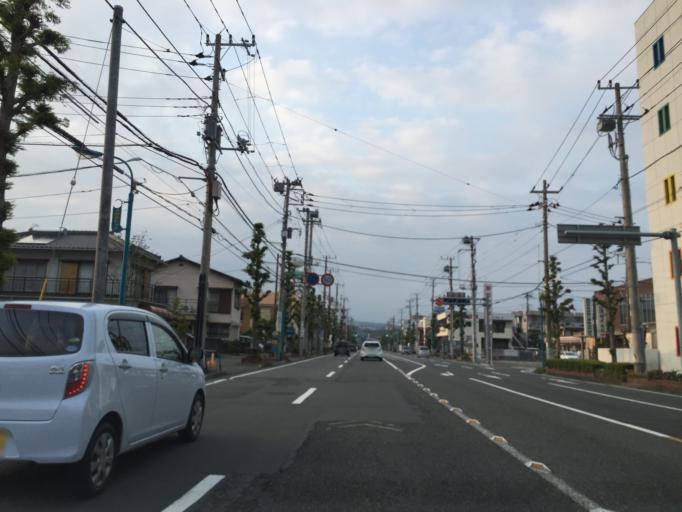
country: JP
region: Shizuoka
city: Numazu
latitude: 35.1158
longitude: 138.8598
